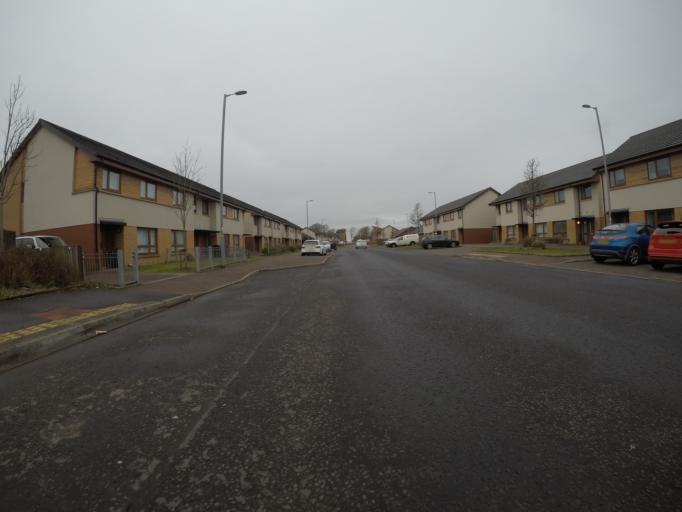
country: GB
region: Scotland
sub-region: North Ayrshire
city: Irvine
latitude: 55.6256
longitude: -4.6696
